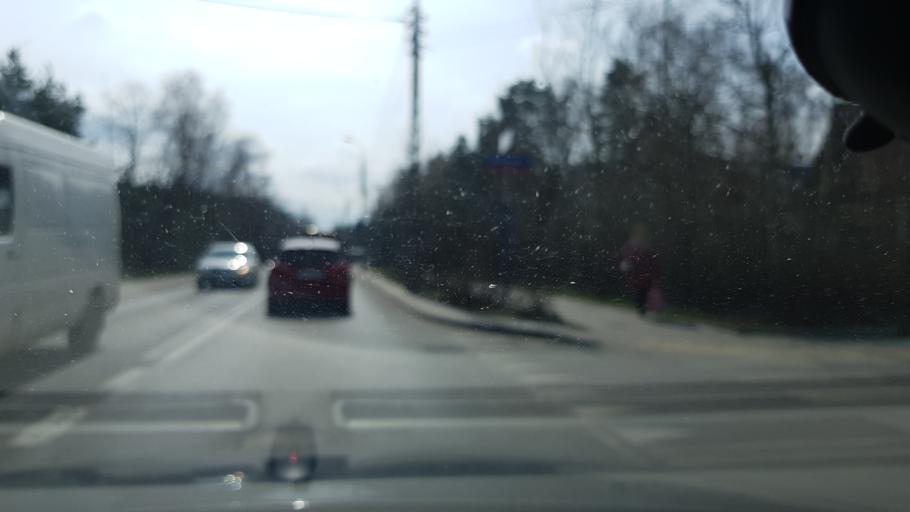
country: PL
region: Masovian Voivodeship
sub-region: Warszawa
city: Wesola
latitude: 52.2442
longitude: 21.2229
